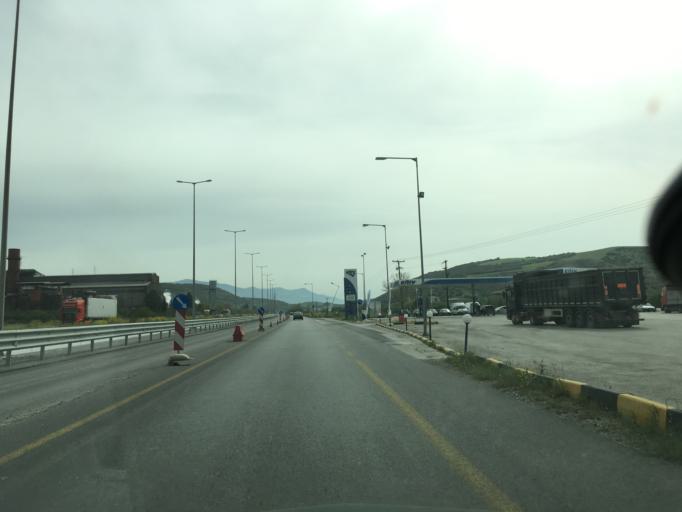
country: GR
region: Thessaly
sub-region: Nomos Magnisias
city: Velestino
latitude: 39.3848
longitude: 22.8015
